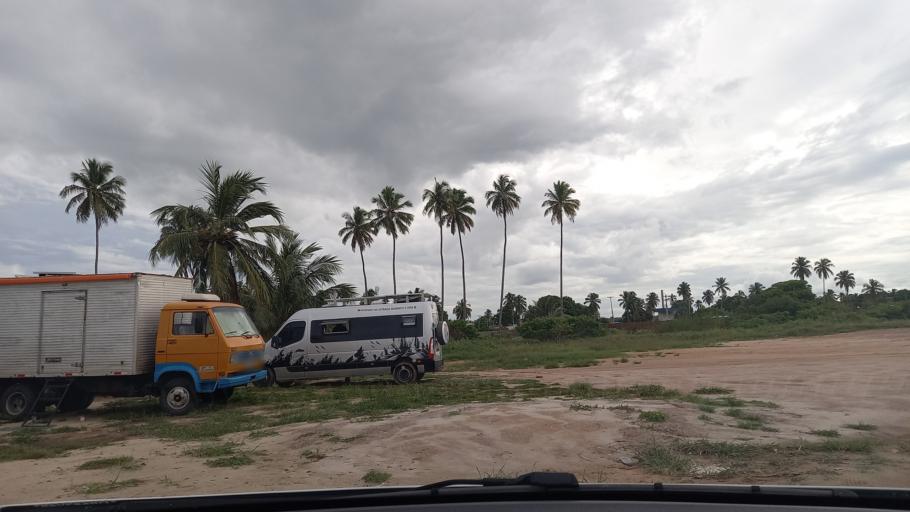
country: BR
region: Pernambuco
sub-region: Sao Jose Da Coroa Grande
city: Sao Jose da Coroa Grande
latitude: -8.9219
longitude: -35.1568
